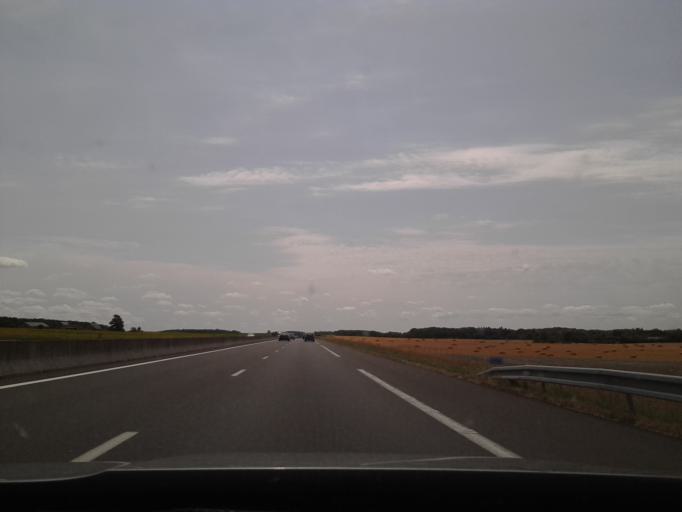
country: FR
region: Centre
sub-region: Departement d'Indre-et-Loire
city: Saint-Paterne-Racan
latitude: 47.6104
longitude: 0.5274
